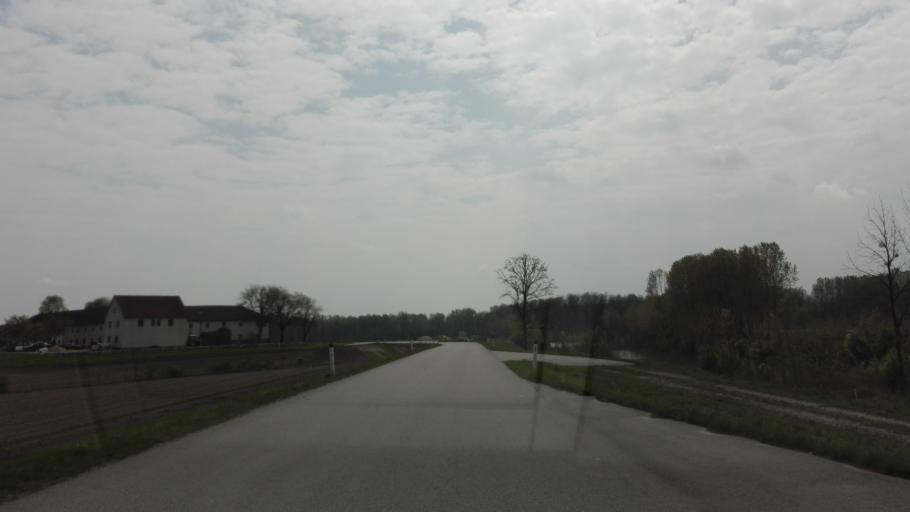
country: AT
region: Upper Austria
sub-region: Politischer Bezirk Perg
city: Perg
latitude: 48.1955
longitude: 14.6314
